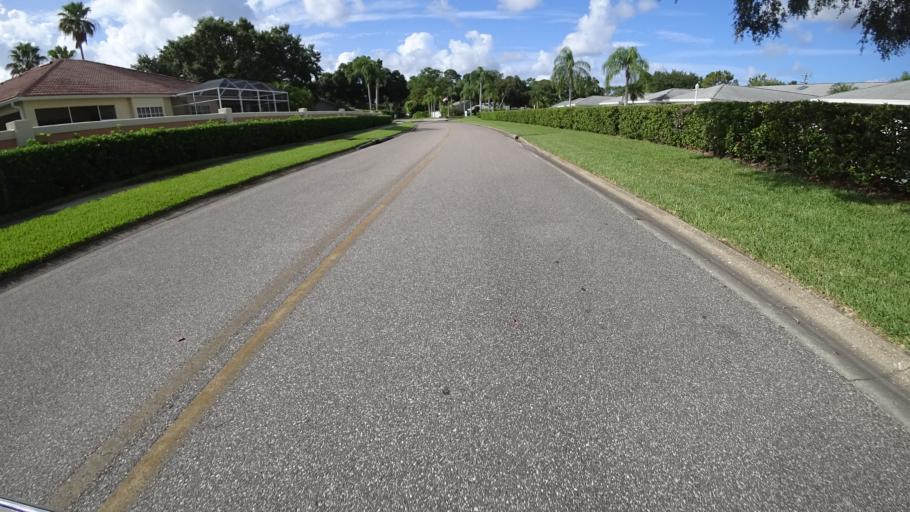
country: US
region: Florida
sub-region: Sarasota County
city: Desoto Lakes
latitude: 27.4037
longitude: -82.4885
